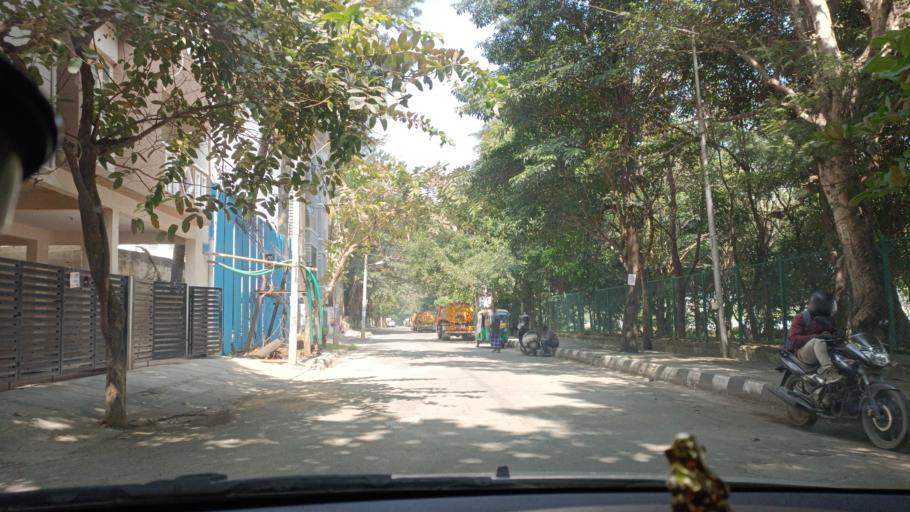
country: IN
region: Karnataka
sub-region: Bangalore Urban
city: Bangalore
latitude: 12.9099
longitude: 77.6153
